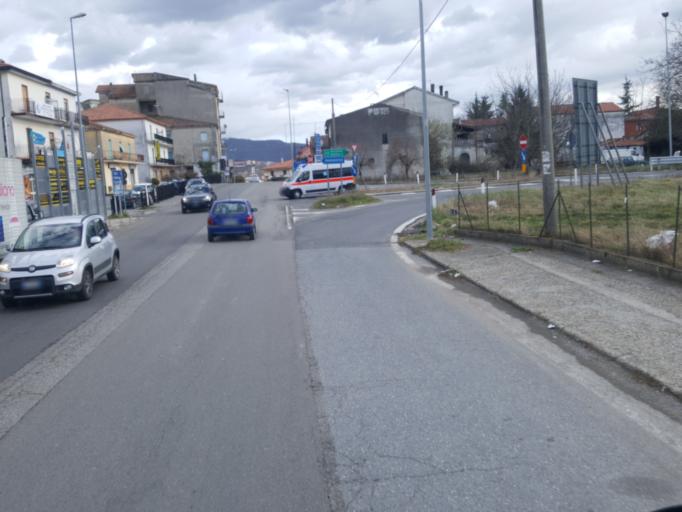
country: IT
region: Calabria
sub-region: Provincia di Cosenza
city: Santo Stefano di Rogliano
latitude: 39.1998
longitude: 16.3136
